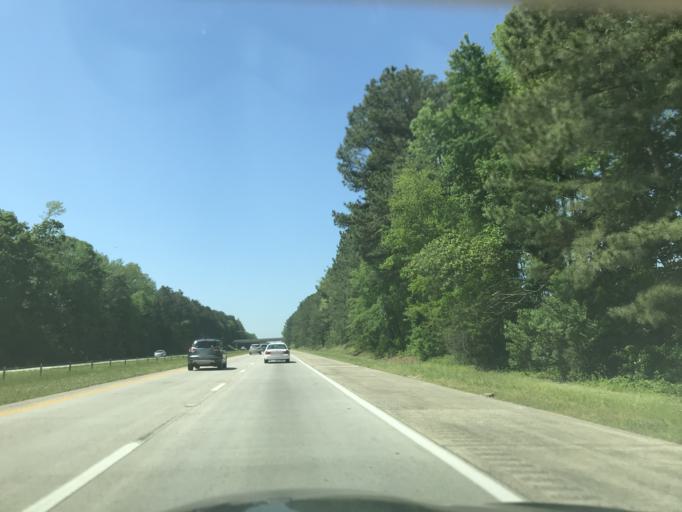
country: US
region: North Carolina
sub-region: Johnston County
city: Benson
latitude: 35.5289
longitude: -78.5666
